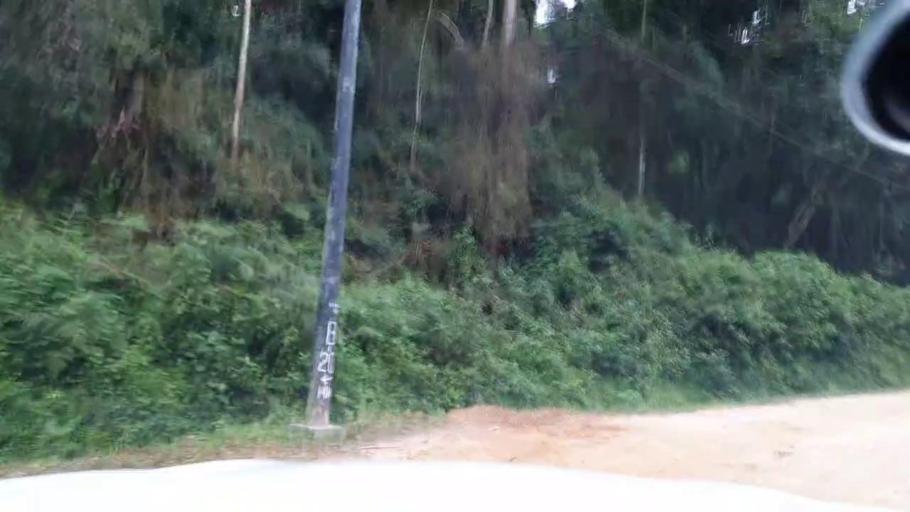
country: RW
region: Western Province
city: Cyangugu
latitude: -2.5694
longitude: 29.2255
